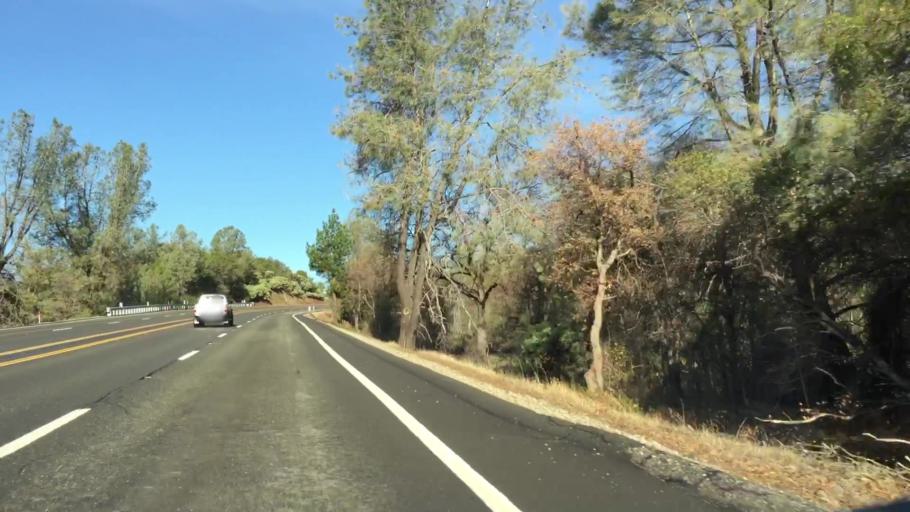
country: US
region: California
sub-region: Butte County
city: Paradise
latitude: 39.6786
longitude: -121.5452
